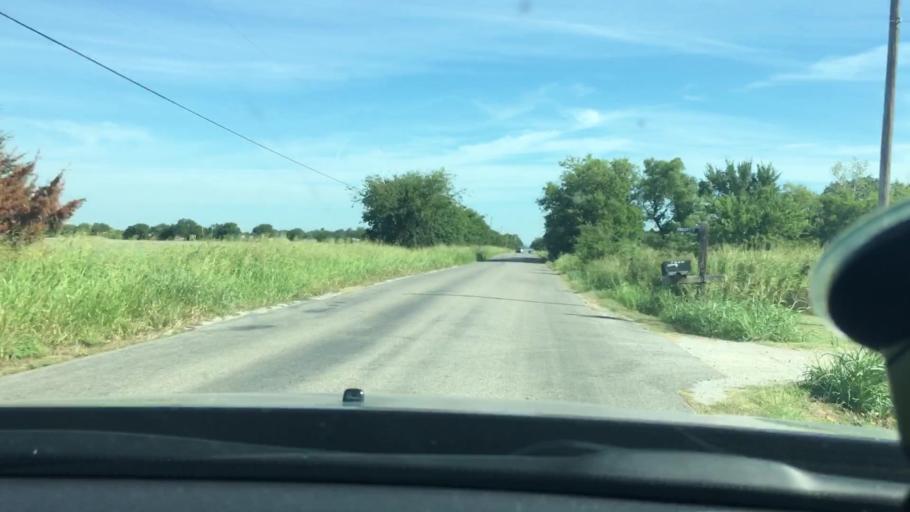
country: US
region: Oklahoma
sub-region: Carter County
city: Lone Grove
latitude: 34.1934
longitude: -97.2475
